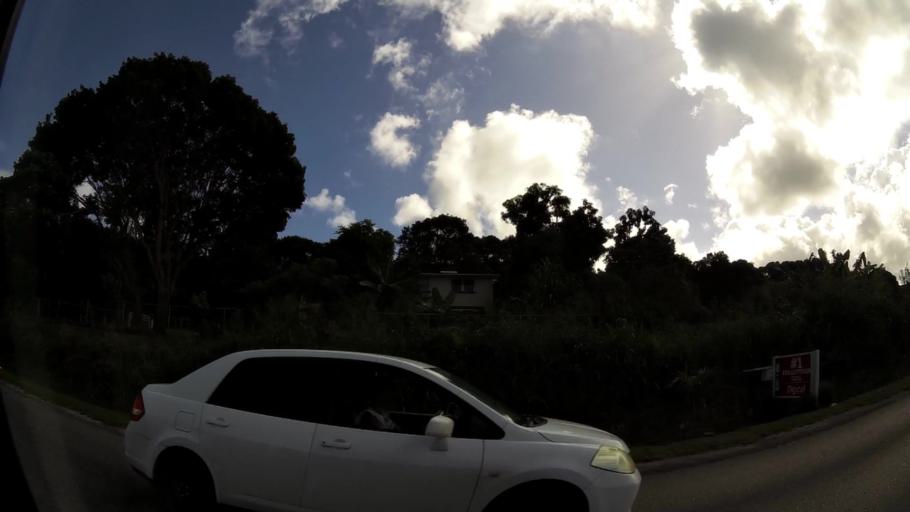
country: BB
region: Saint James
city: Holetown
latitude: 13.1931
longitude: -59.6122
